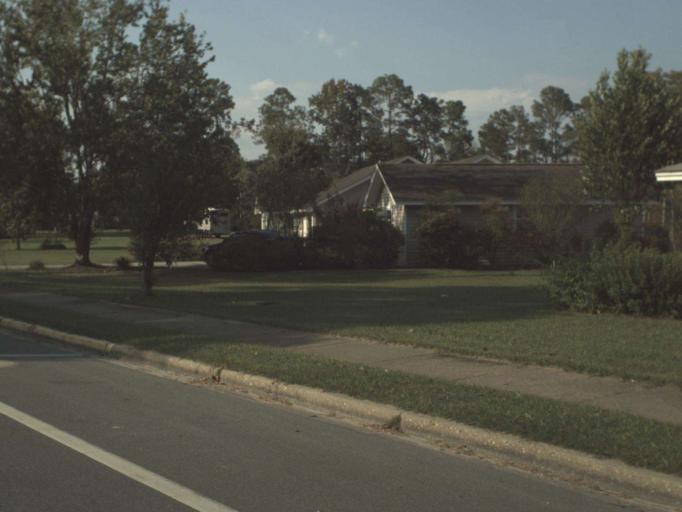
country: US
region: Florida
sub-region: Gulf County
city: Wewahitchka
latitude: 30.1140
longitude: -85.2034
